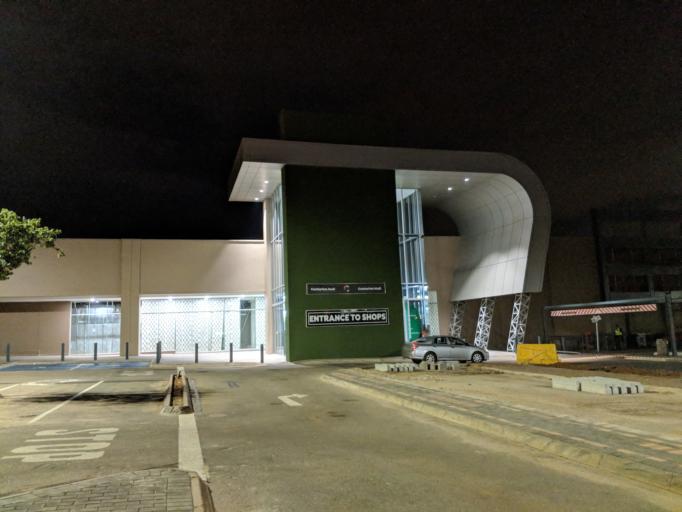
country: ZA
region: Gauteng
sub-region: City of Tshwane Metropolitan Municipality
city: Centurion
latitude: -25.8584
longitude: 28.1881
